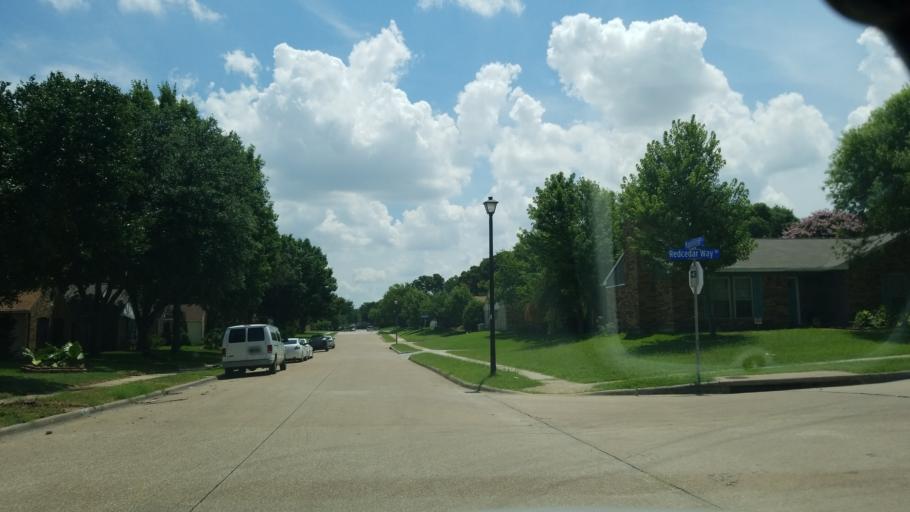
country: US
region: Texas
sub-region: Dallas County
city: Coppell
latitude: 32.9678
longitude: -96.9641
